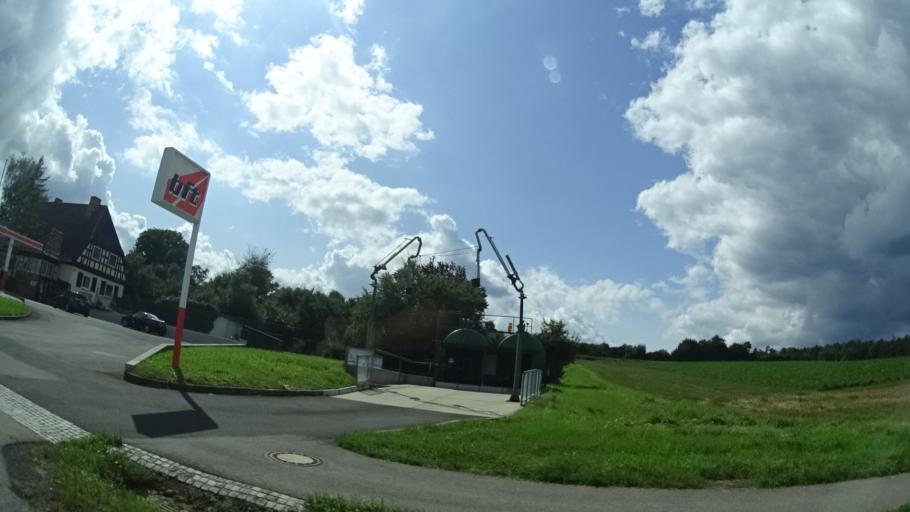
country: DE
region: Bavaria
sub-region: Regierungsbezirk Unterfranken
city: Rentweinsdorf
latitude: 50.0494
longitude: 10.8110
